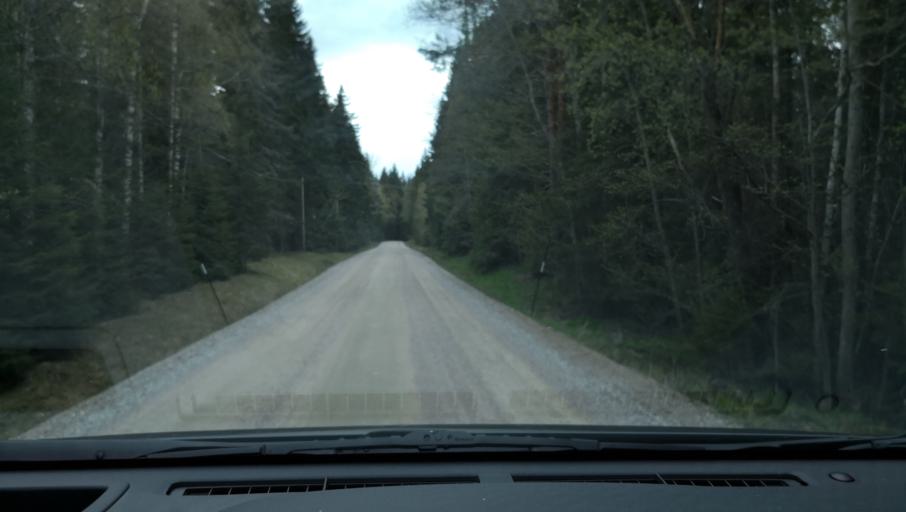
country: SE
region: Vaestmanland
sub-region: Fagersta Kommun
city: Fagersta
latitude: 60.0915
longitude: 15.7966
